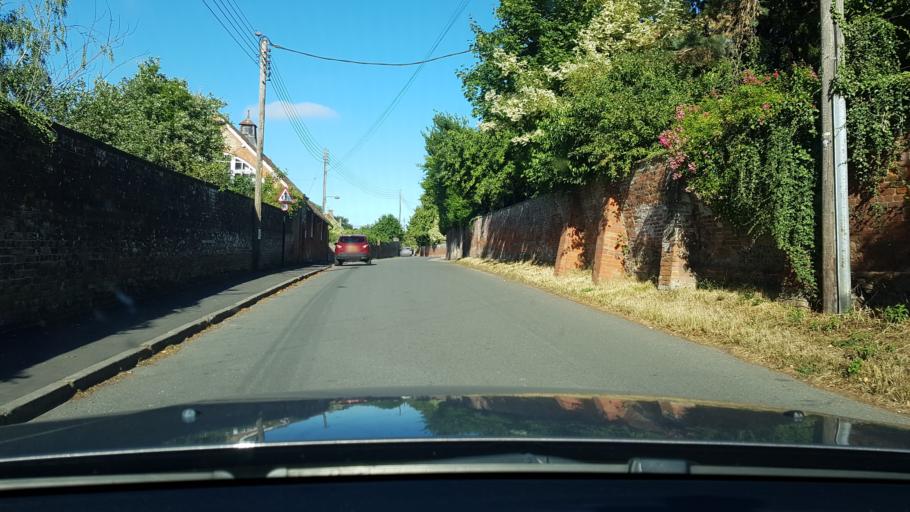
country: GB
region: England
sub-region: Wiltshire
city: Ramsbury
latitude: 51.4435
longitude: -1.6070
